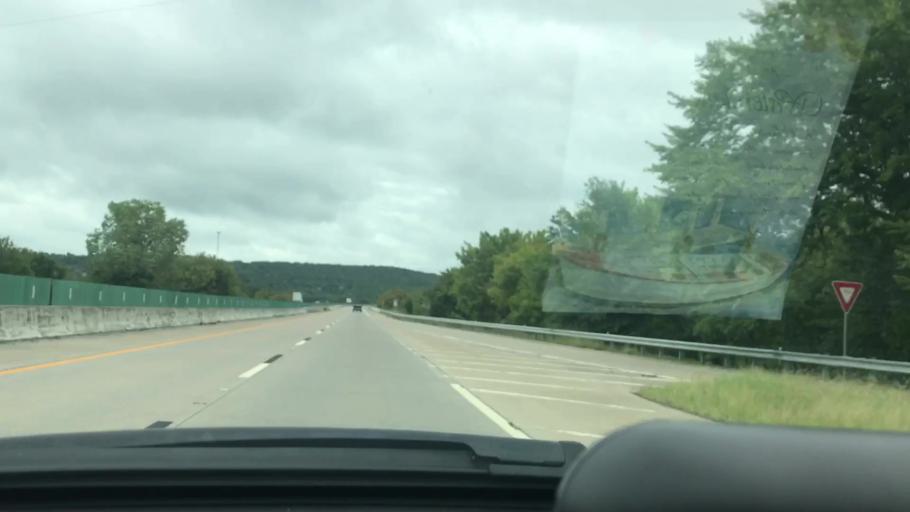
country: US
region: Oklahoma
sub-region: Pittsburg County
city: Krebs
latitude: 35.1039
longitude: -95.6955
